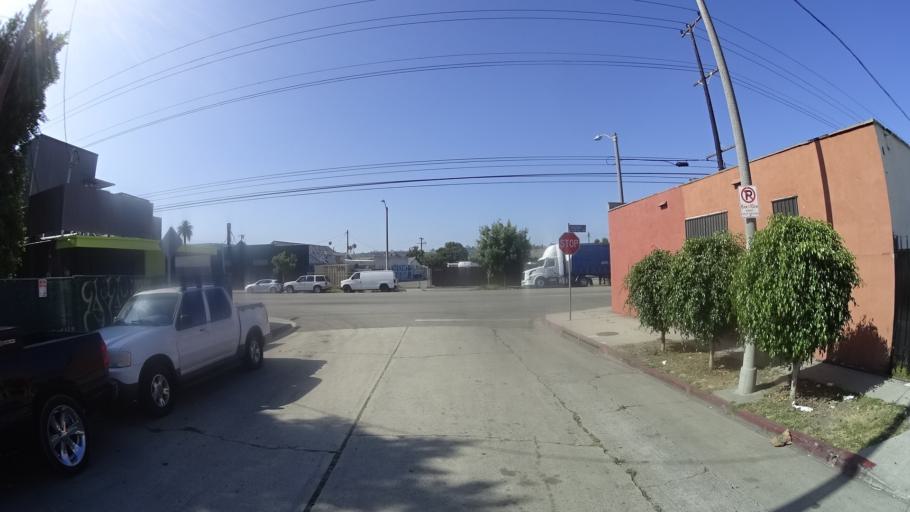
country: US
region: California
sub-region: Los Angeles County
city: Culver City
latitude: 34.0328
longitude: -118.3648
